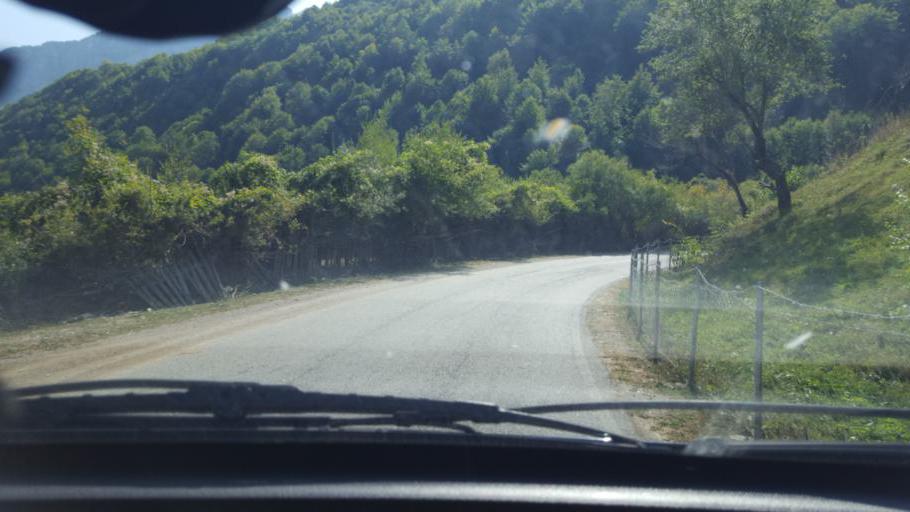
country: ME
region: Andrijevica
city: Andrijevica
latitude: 42.5823
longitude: 19.7348
